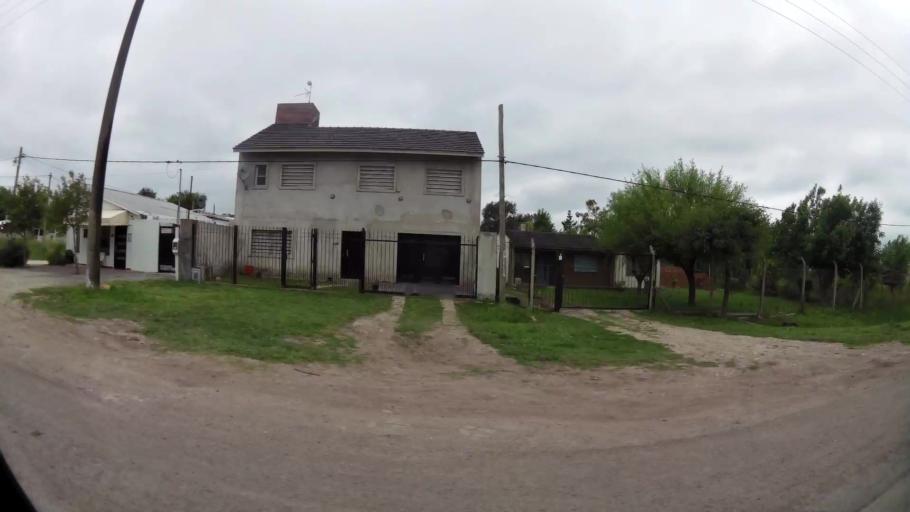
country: AR
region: Buenos Aires
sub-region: Partido de La Plata
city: La Plata
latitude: -35.0237
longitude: -58.0793
